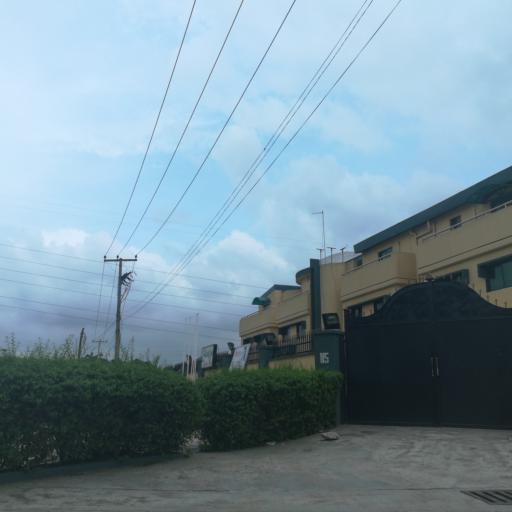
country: NG
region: Lagos
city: Ojota
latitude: 6.5769
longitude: 3.3893
